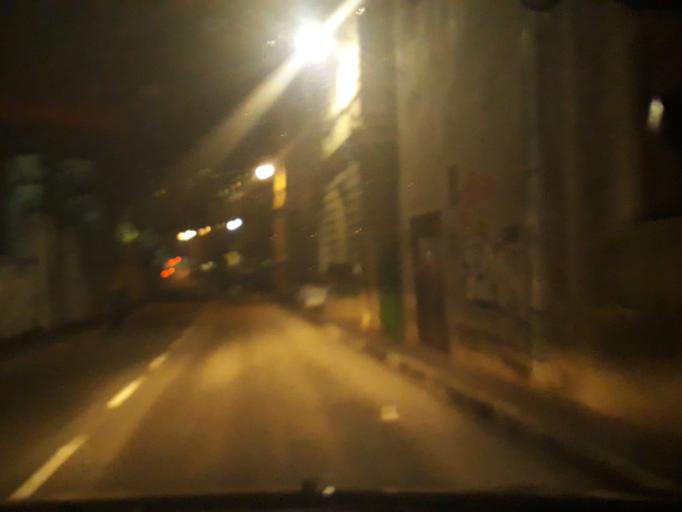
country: BA
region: Federation of Bosnia and Herzegovina
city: Kobilja Glava
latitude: 43.8566
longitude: 18.4311
